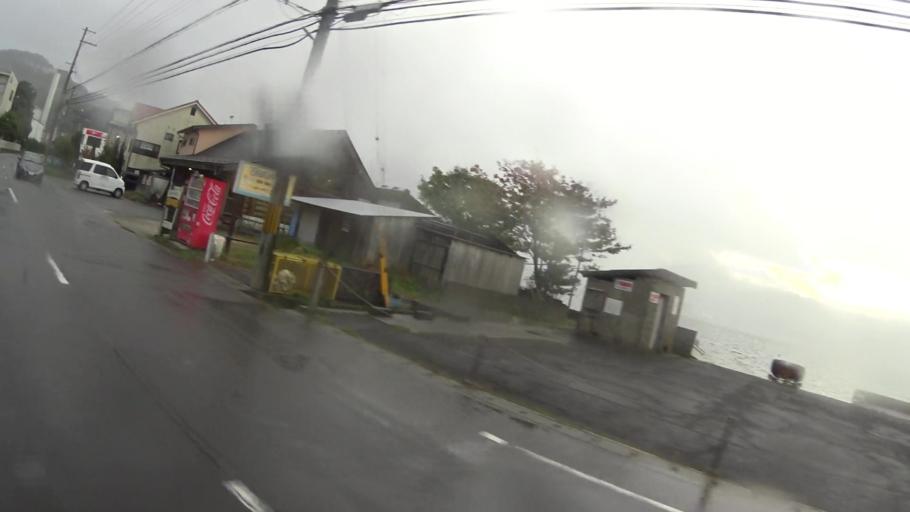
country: JP
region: Kyoto
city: Miyazu
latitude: 35.5523
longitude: 135.2103
